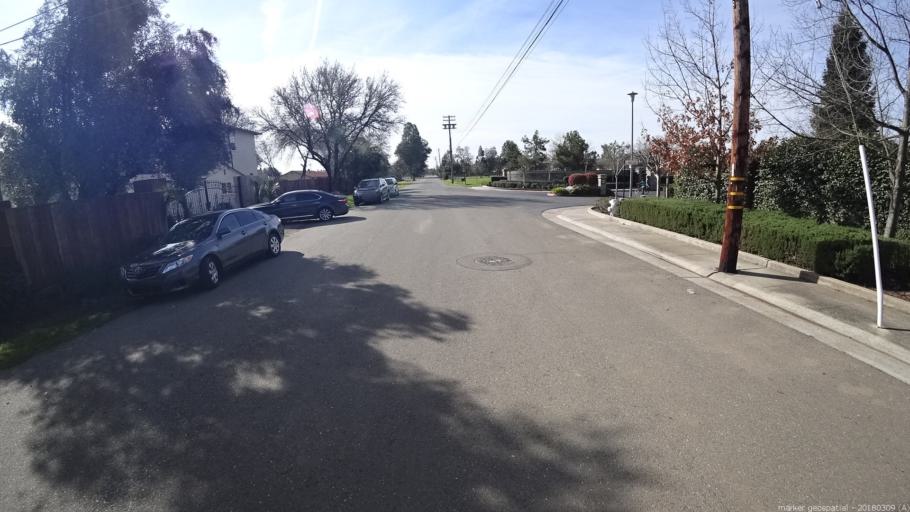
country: US
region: California
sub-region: Sacramento County
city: Florin
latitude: 38.4574
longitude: -121.3902
